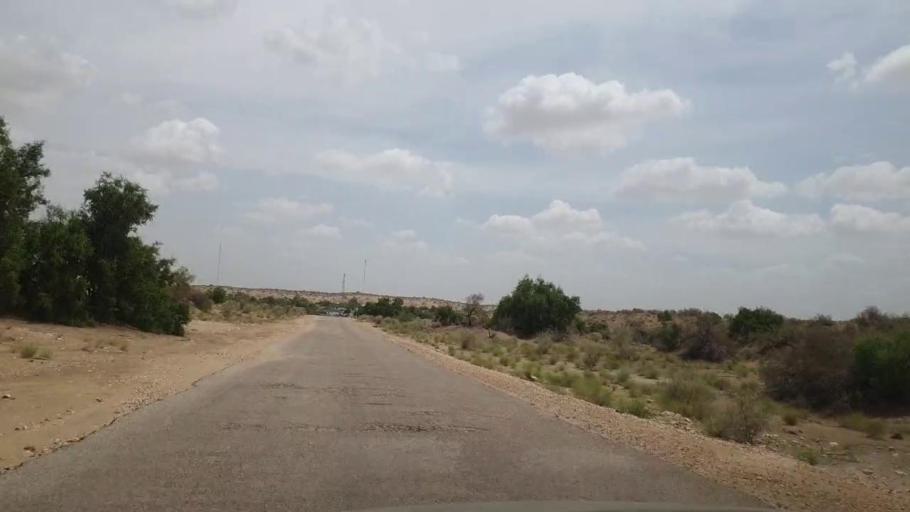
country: PK
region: Sindh
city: Kot Diji
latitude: 27.1398
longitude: 69.2251
